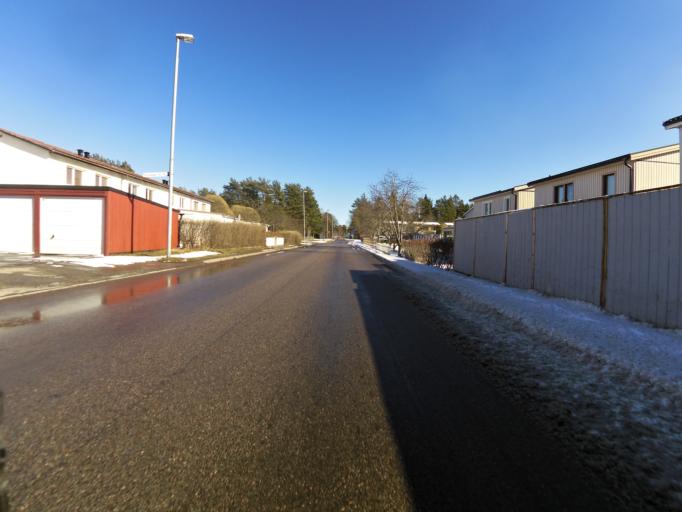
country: SE
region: Gaevleborg
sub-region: Gavle Kommun
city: Gavle
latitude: 60.6628
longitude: 17.2216
